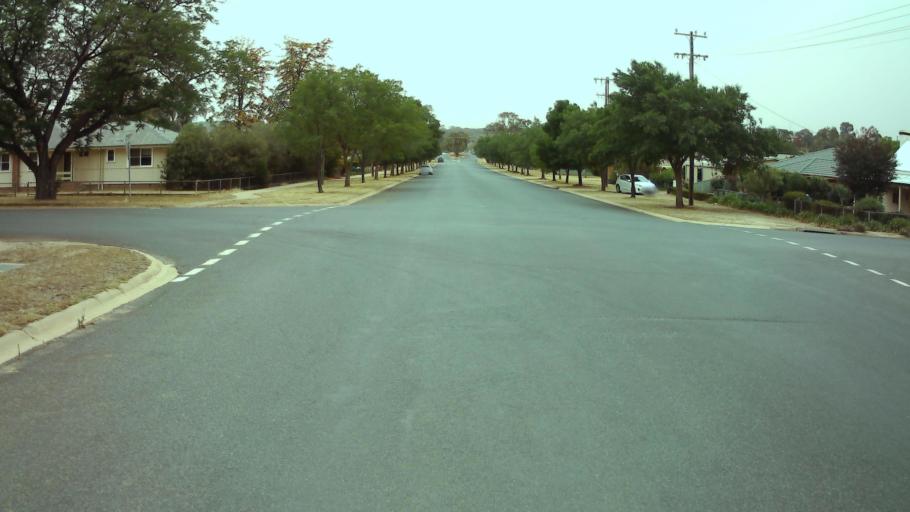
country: AU
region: New South Wales
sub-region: Weddin
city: Grenfell
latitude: -33.8982
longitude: 148.1651
